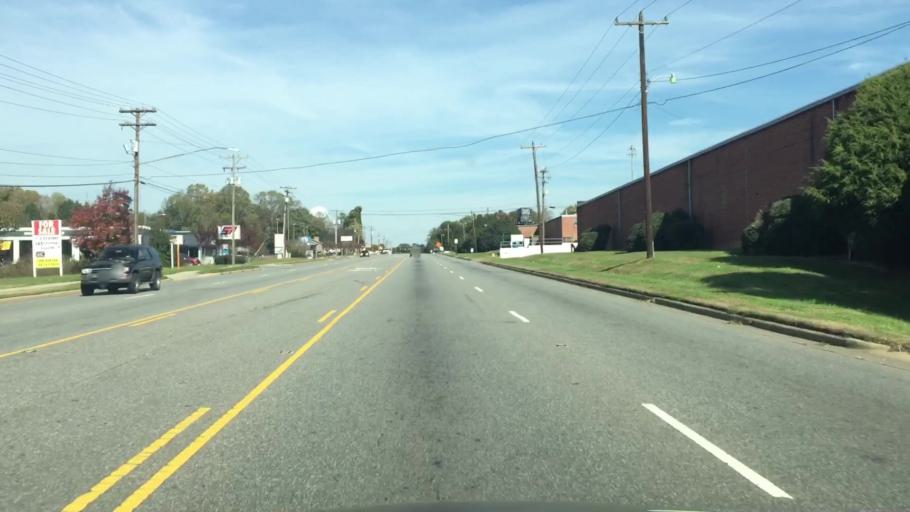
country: US
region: North Carolina
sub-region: Iredell County
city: Mooresville
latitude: 35.5918
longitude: -80.8222
